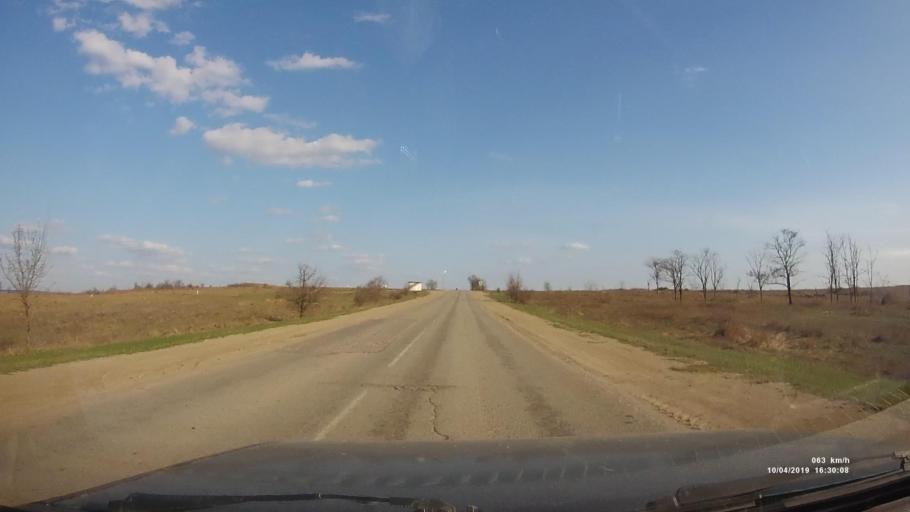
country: RU
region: Rostov
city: Staraya Stanitsa
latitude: 48.2642
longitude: 40.3624
